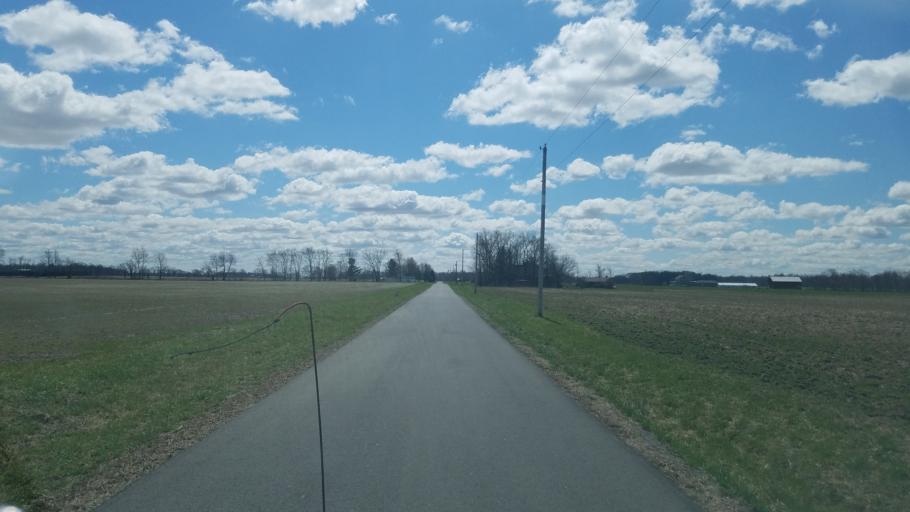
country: US
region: Ohio
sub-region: Hancock County
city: Findlay
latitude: 40.9733
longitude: -83.5357
